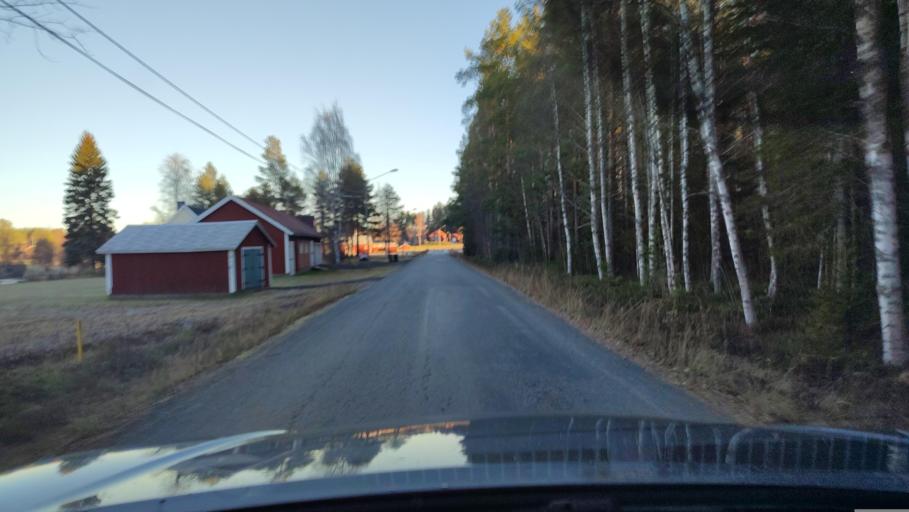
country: SE
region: Vaesterbotten
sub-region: Skelleftea Kommun
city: Soedra Bergsbyn
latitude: 64.6309
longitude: 21.0591
